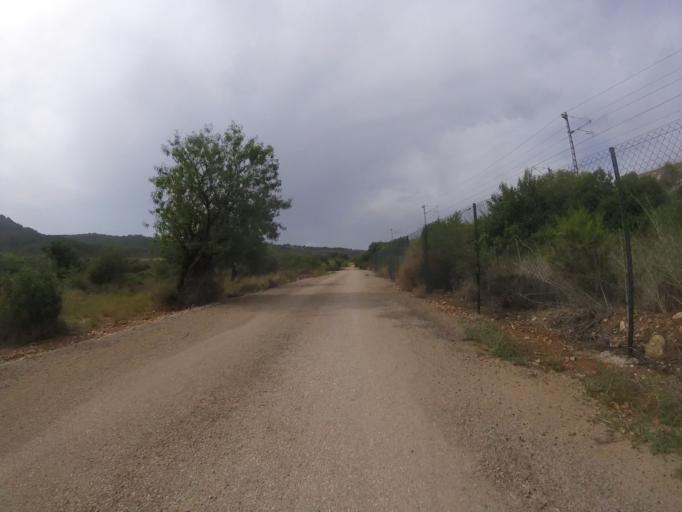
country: ES
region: Valencia
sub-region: Provincia de Castello
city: Alcoceber
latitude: 40.2625
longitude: 0.2552
